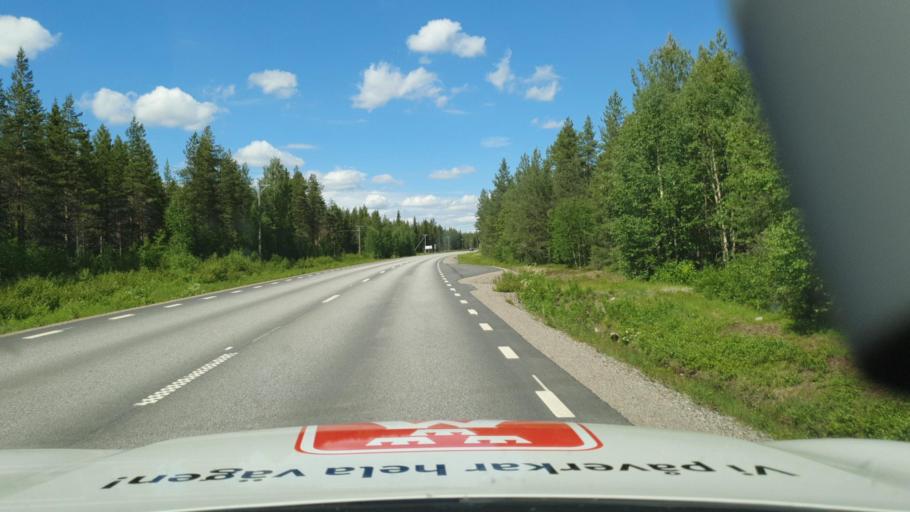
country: SE
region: Vaesterbotten
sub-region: Skelleftea Kommun
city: Langsele
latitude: 64.9451
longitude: 20.2729
